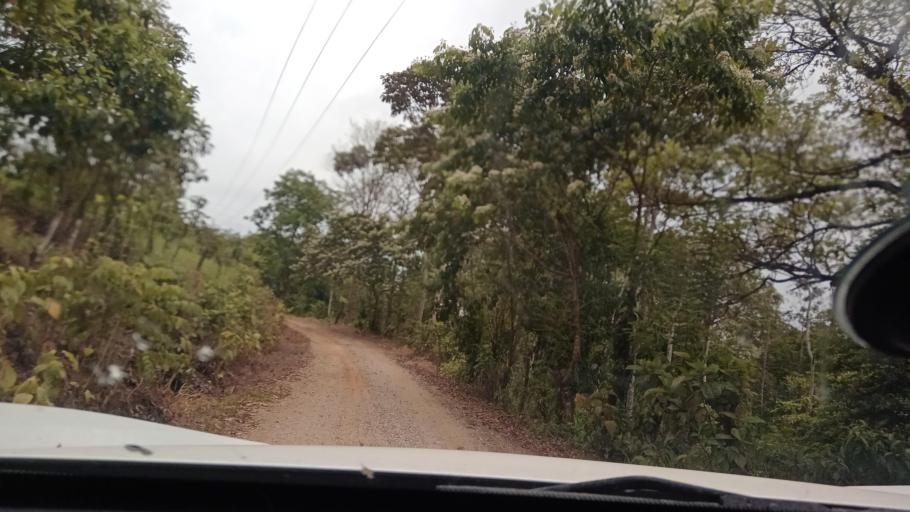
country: MX
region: Veracruz
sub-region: Uxpanapa
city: Poblado 10
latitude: 17.4482
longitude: -94.0909
